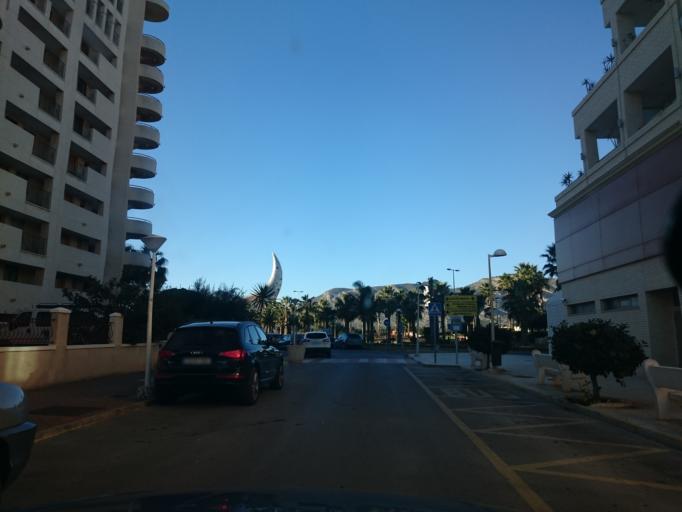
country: ES
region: Valencia
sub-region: Provincia de Castello
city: Orpesa/Oropesa del Mar
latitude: 40.1080
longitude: 0.1498
